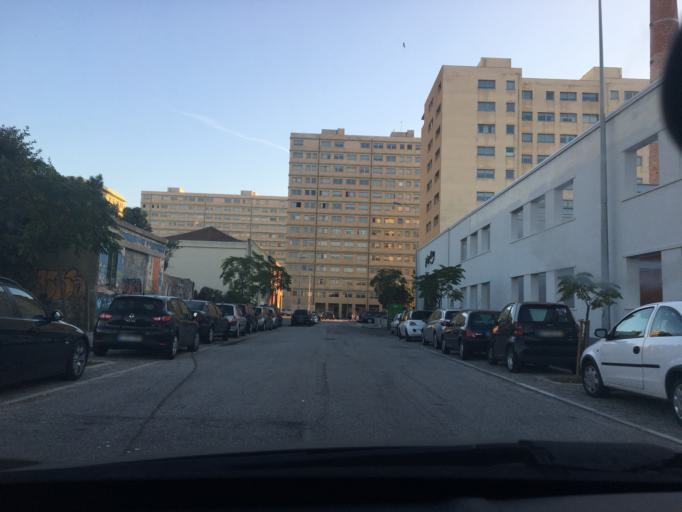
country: PT
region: Porto
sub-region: Matosinhos
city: Matosinhos
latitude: 41.1758
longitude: -8.6881
